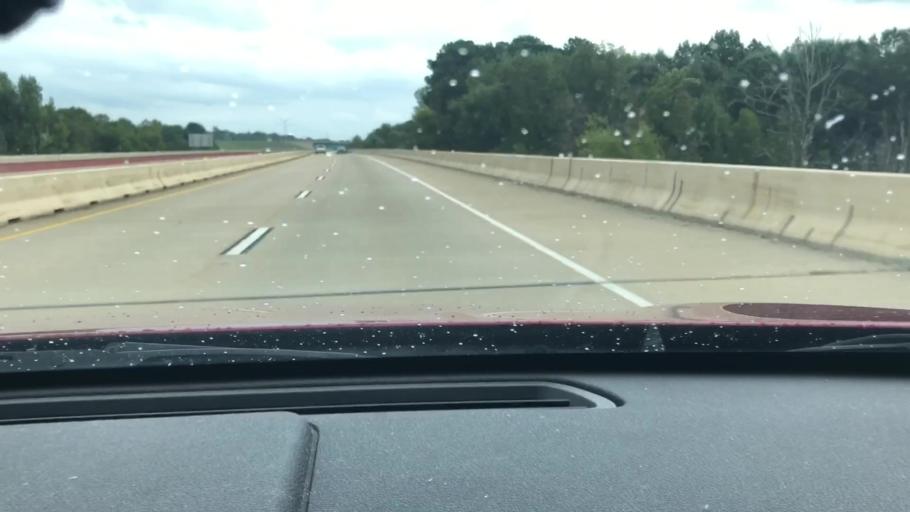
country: US
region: Texas
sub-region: Bowie County
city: Texarkana
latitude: 33.3848
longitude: -94.0539
